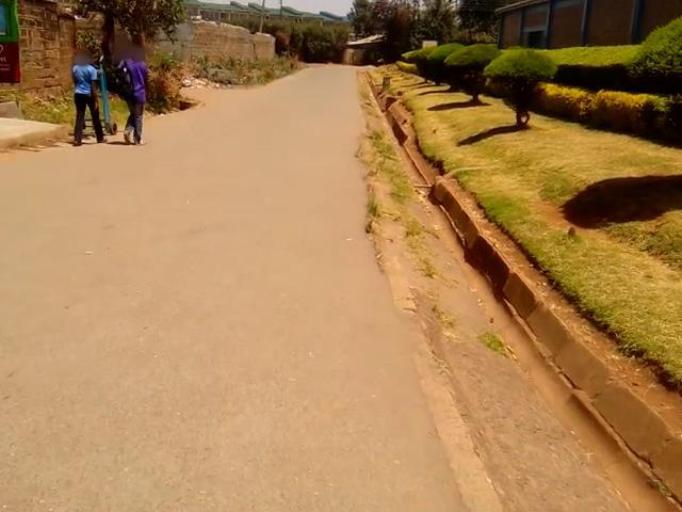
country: KE
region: Nairobi Area
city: Nairobi
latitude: -1.3121
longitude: 36.7760
